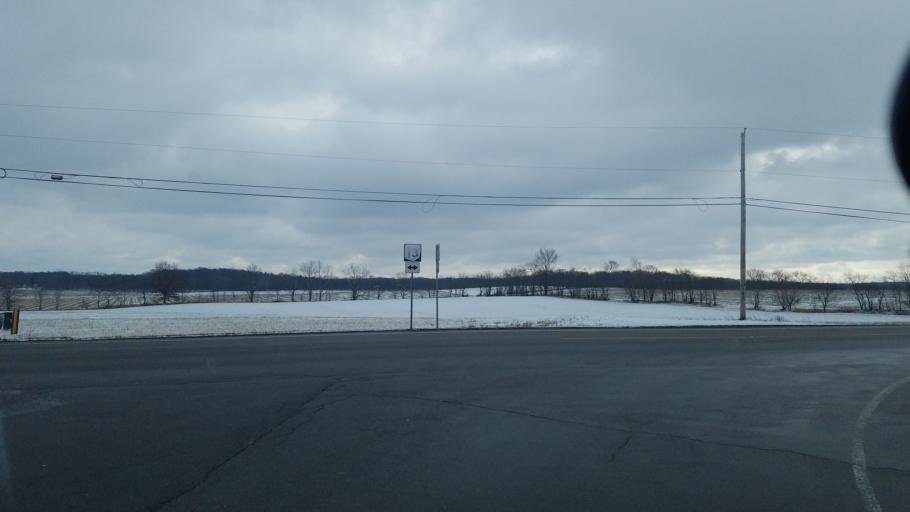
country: US
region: Ohio
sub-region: Knox County
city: Fredericktown
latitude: 40.5236
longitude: -82.5480
